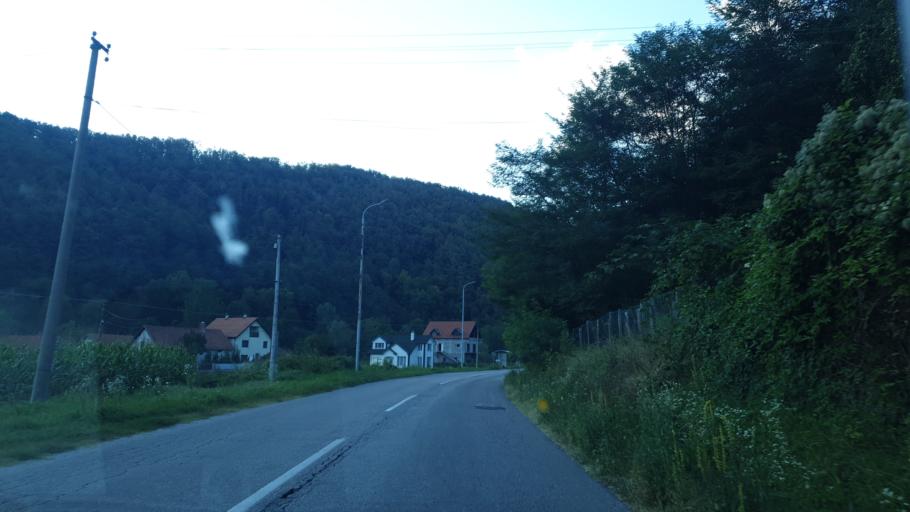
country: RS
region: Central Serbia
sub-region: Zlatiborski Okrug
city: Pozega
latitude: 43.9303
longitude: 20.0031
